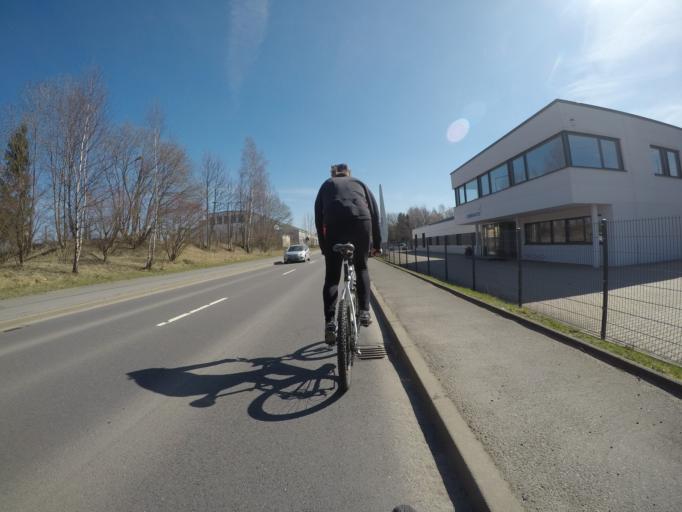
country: DE
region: Saxony
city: Freiberg
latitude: 50.9062
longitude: 13.3618
